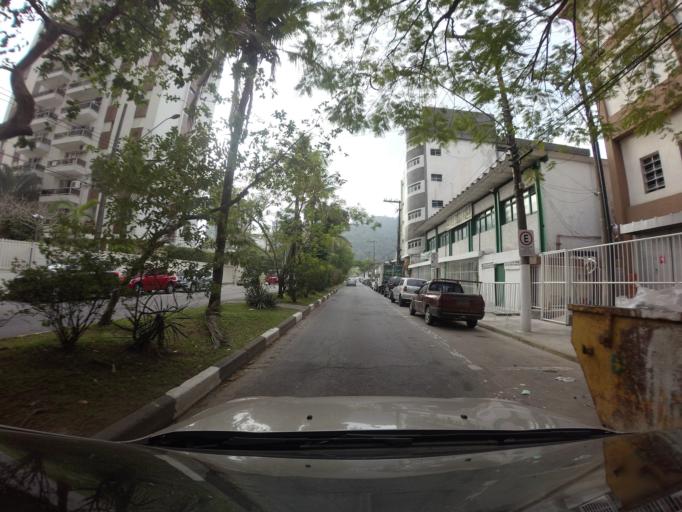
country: BR
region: Sao Paulo
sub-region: Guaruja
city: Guaruja
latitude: -23.9928
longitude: -46.2540
